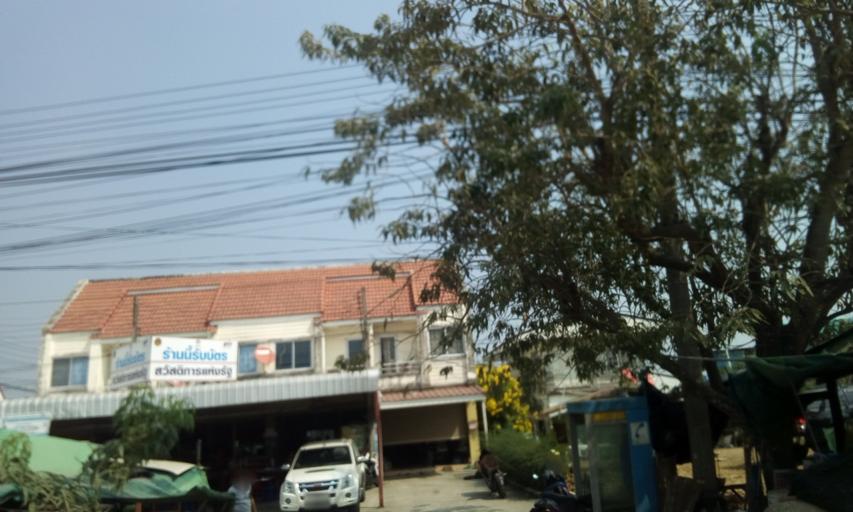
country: TH
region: Pathum Thani
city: Ban Lam Luk Ka
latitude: 13.9751
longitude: 100.7525
